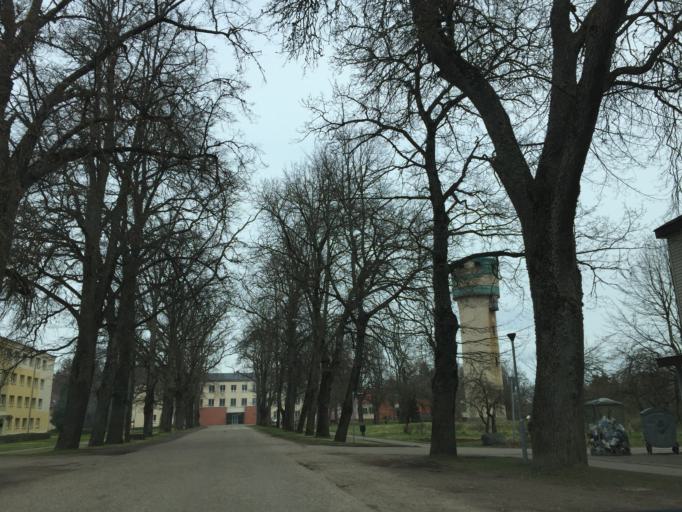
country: LV
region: Priekuli
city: Priekuli
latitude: 57.3530
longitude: 25.3321
